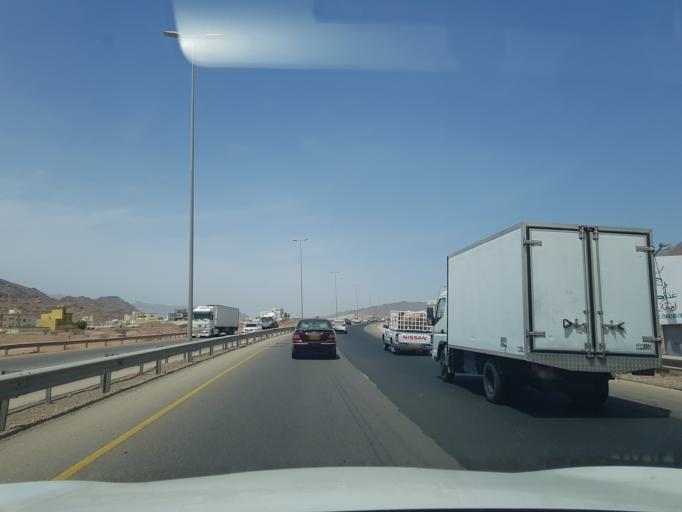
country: OM
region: Muhafazat ad Dakhiliyah
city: Bidbid
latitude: 23.4586
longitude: 58.1701
